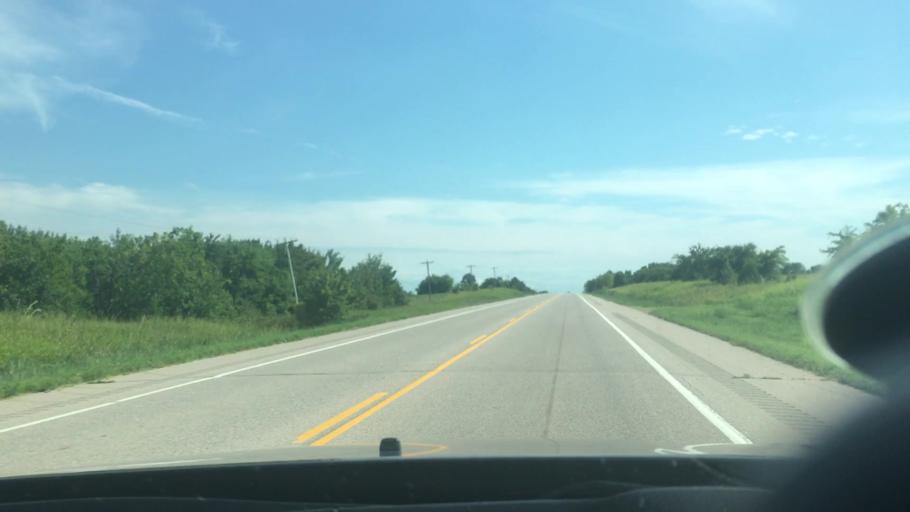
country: US
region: Oklahoma
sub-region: Seminole County
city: Konawa
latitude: 34.9794
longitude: -96.6792
